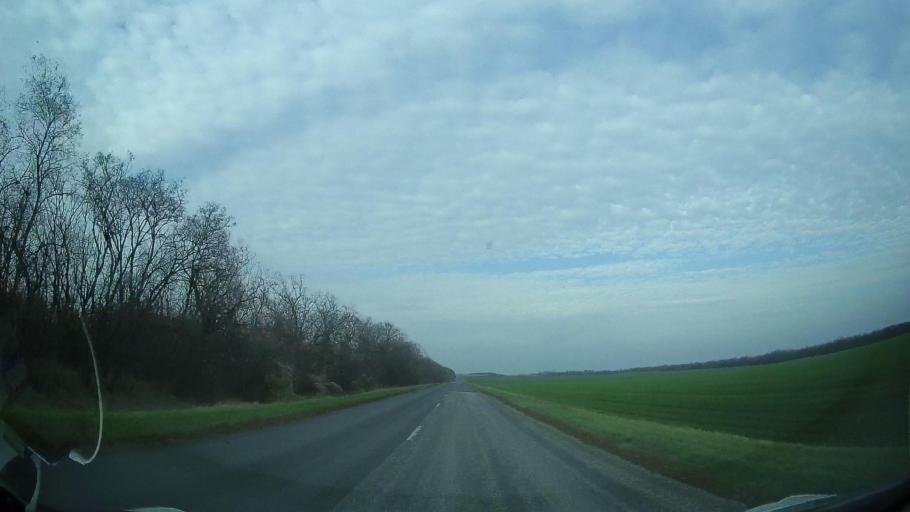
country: RU
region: Rostov
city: Zernograd
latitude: 46.9538
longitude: 40.3668
